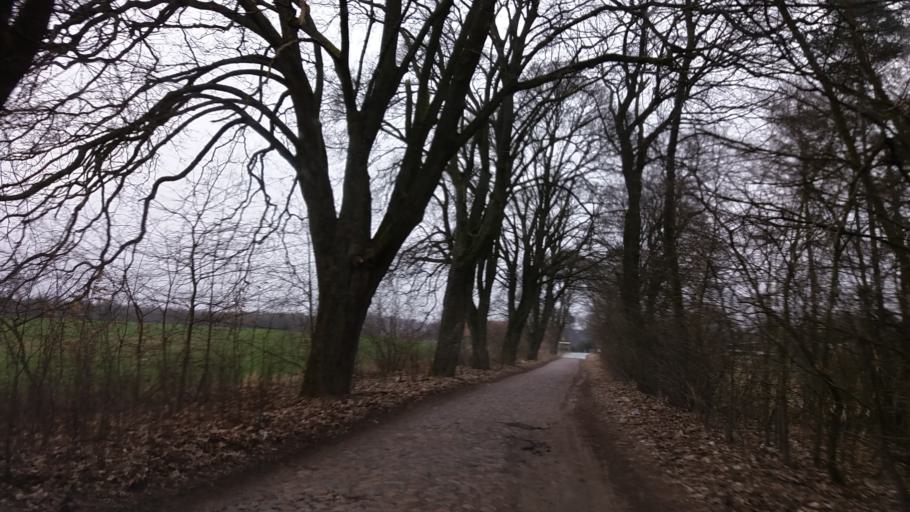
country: PL
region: West Pomeranian Voivodeship
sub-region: Powiat choszczenski
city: Choszczno
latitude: 53.1936
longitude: 15.3503
